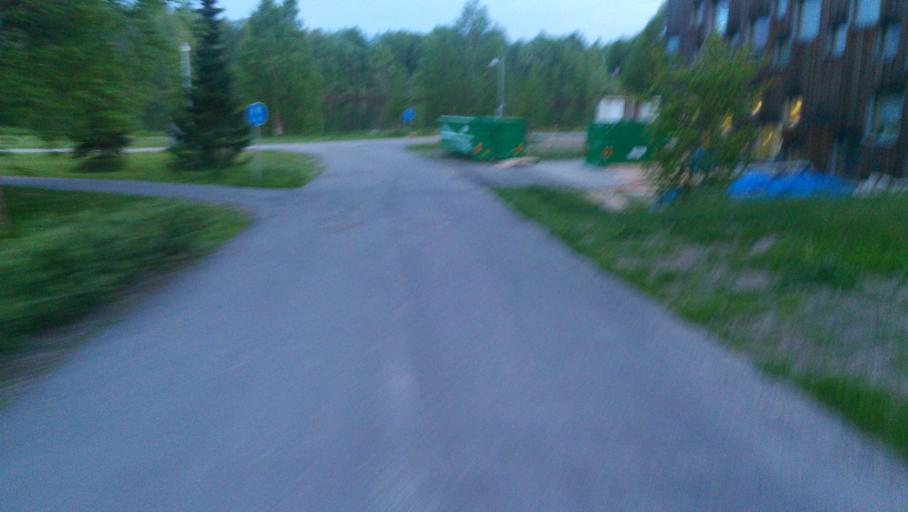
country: SE
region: Vaesterbotten
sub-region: Umea Kommun
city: Umea
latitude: 63.8204
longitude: 20.2782
